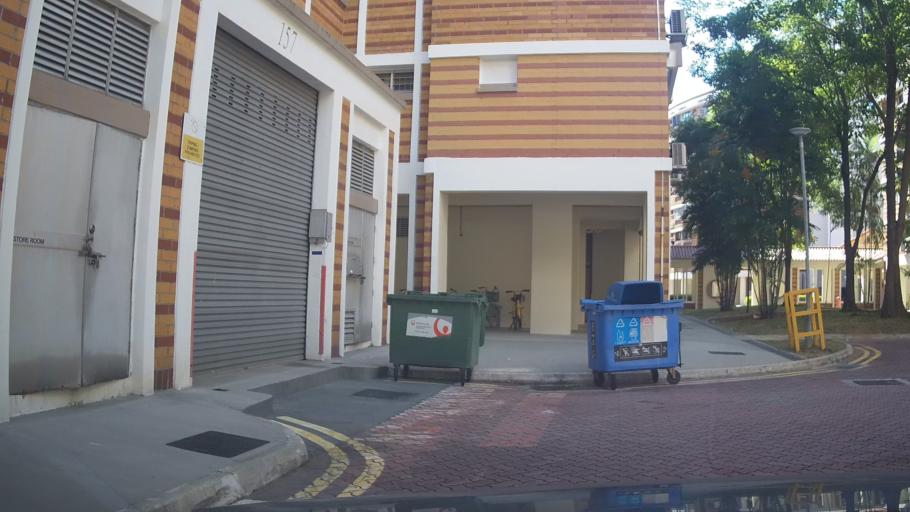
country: SG
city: Singapore
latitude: 1.3645
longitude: 103.9624
